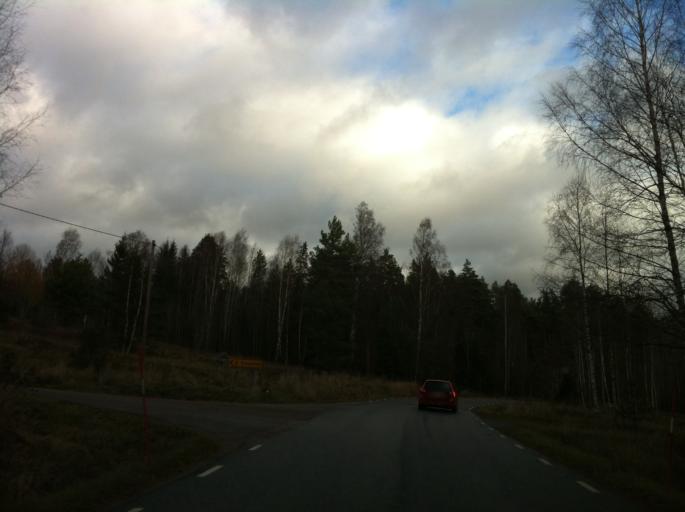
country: SE
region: Kalmar
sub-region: Hultsfreds Kommun
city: Hultsfred
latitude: 57.5325
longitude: 15.7694
